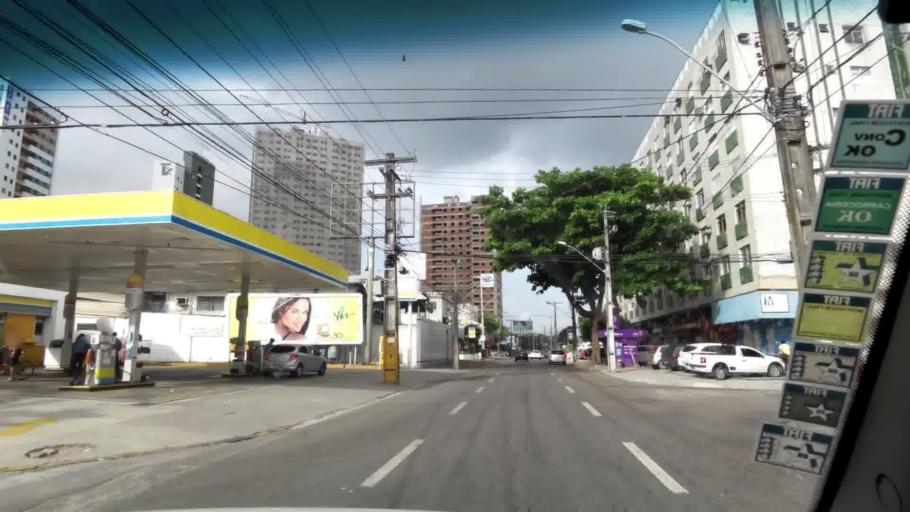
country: BR
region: Pernambuco
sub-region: Recife
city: Recife
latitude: -8.1327
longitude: -34.9080
